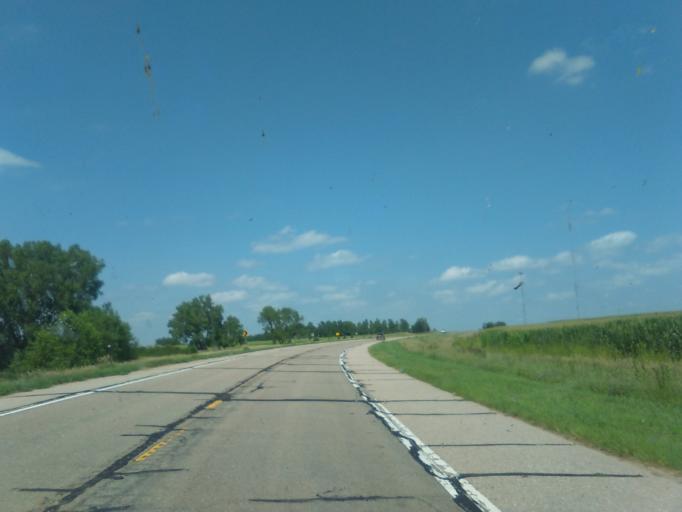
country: US
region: Nebraska
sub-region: Dawson County
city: Lexington
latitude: 40.6963
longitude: -99.7938
